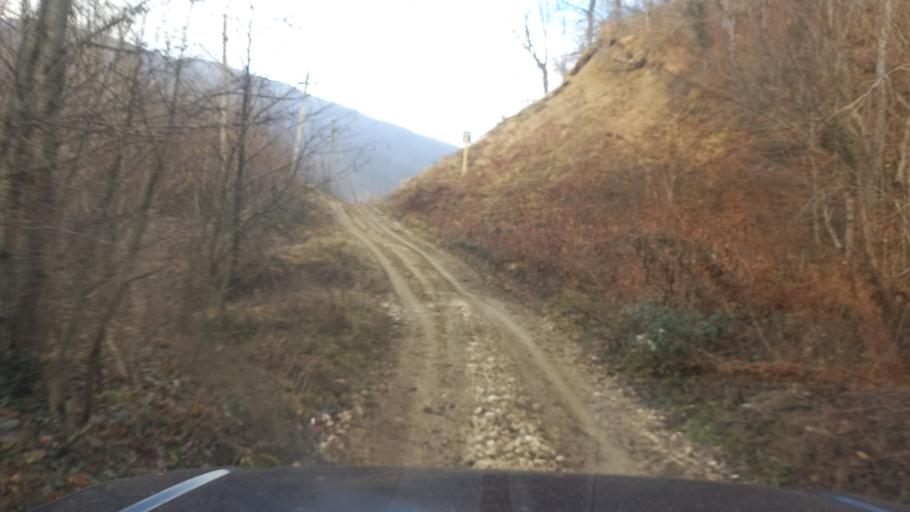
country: RU
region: Krasnodarskiy
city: Neftegorsk
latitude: 44.2074
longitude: 39.7094
